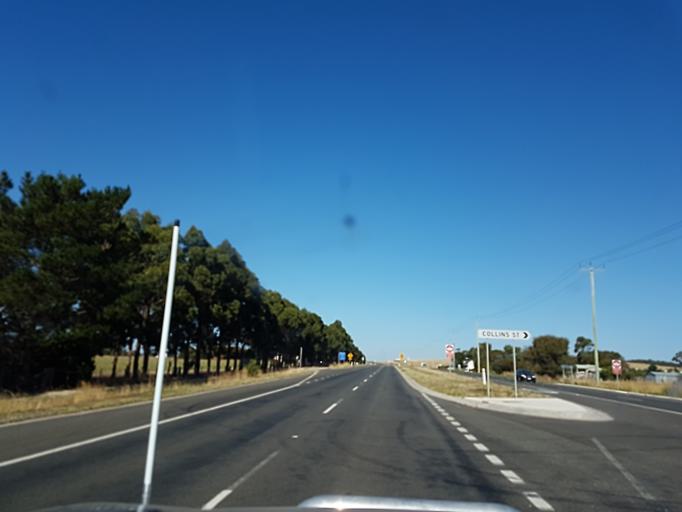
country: AU
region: Victoria
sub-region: Surf Coast
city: Anglesea
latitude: -38.2349
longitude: 144.0081
